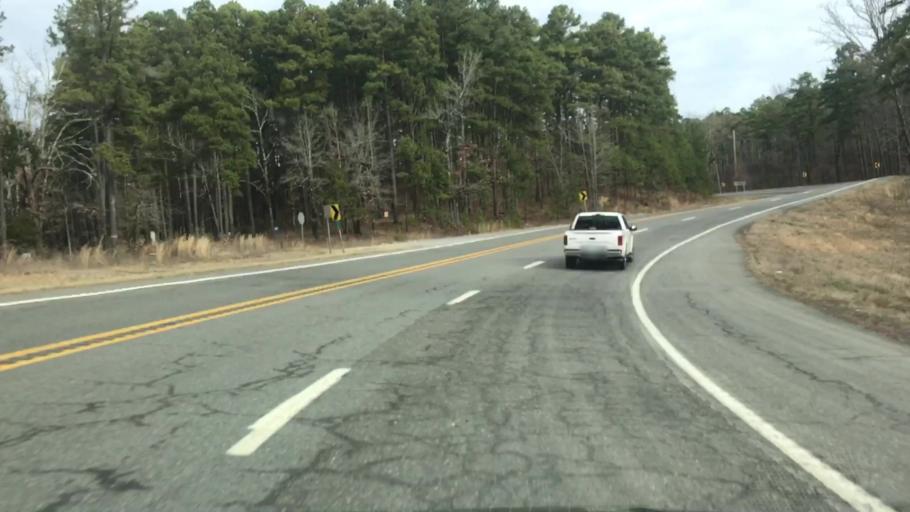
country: US
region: Arkansas
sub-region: Montgomery County
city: Mount Ida
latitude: 34.5933
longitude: -93.6661
